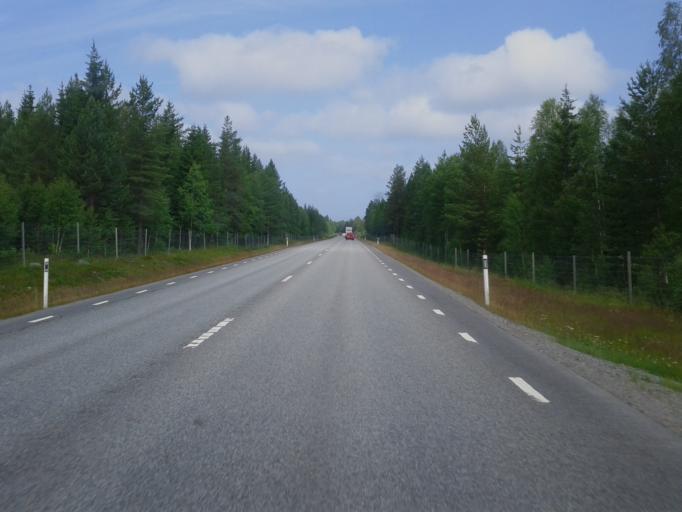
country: SE
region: Vaesterbotten
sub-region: Skelleftea Kommun
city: Burea
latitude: 64.4713
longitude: 21.2921
